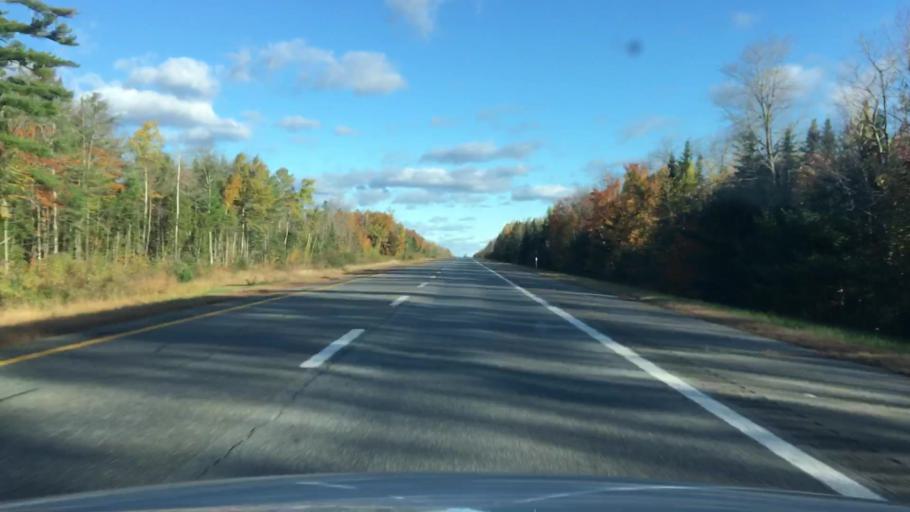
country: US
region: Maine
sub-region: Penobscot County
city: Greenbush
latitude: 45.0740
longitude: -68.6909
